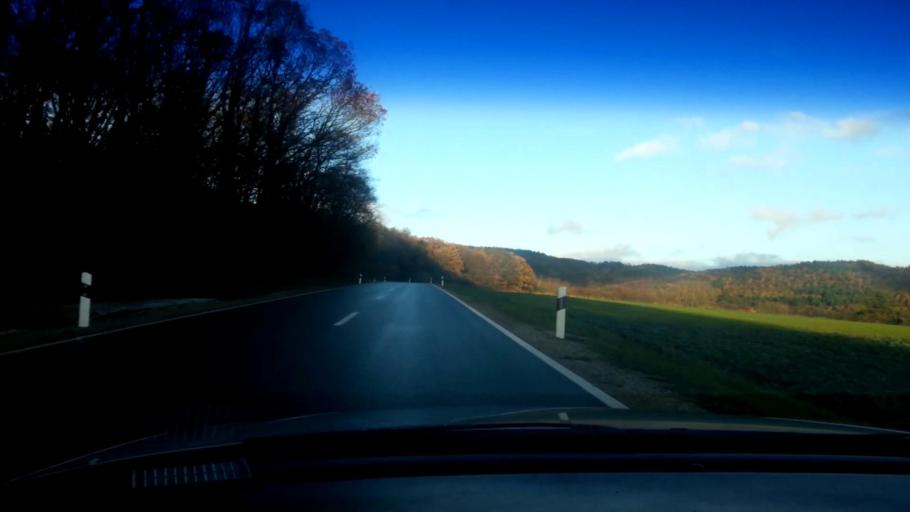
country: DE
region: Bavaria
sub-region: Upper Franconia
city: Buttenheim
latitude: 49.8224
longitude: 11.0460
